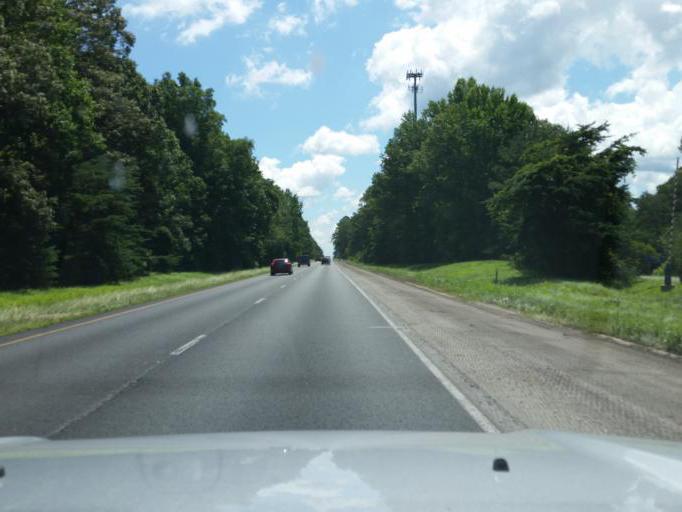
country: US
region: Virginia
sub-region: New Kent County
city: New Kent
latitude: 37.4955
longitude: -77.0275
